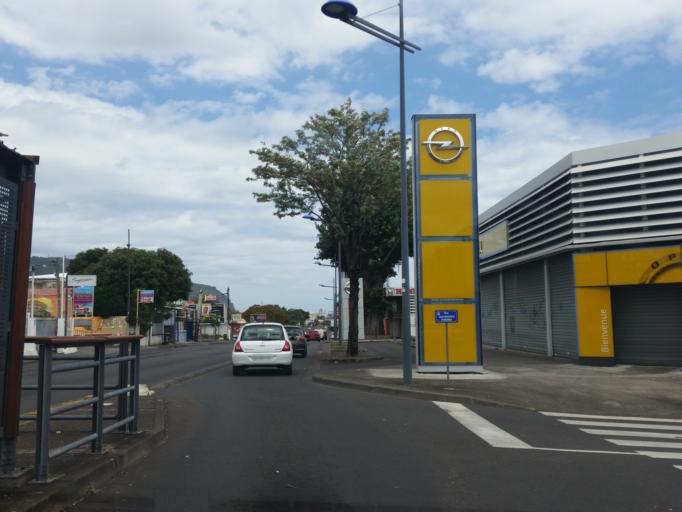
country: RE
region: Reunion
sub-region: Reunion
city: Saint-Denis
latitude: -20.8897
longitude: 55.4774
